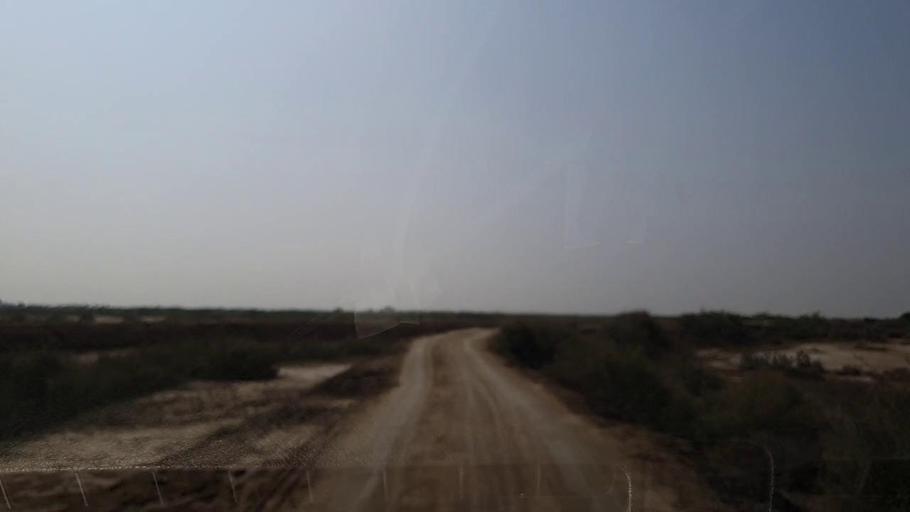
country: PK
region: Sindh
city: Gharo
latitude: 24.6740
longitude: 67.7291
